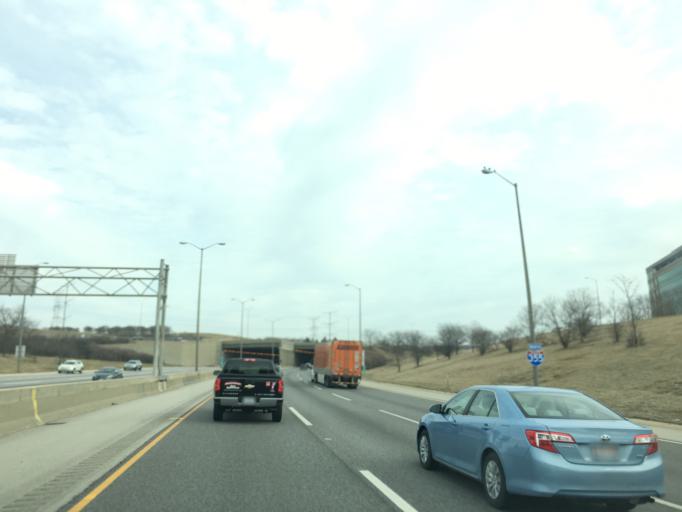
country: US
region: Illinois
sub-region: DuPage County
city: Lisle
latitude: 41.8081
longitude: -88.0526
